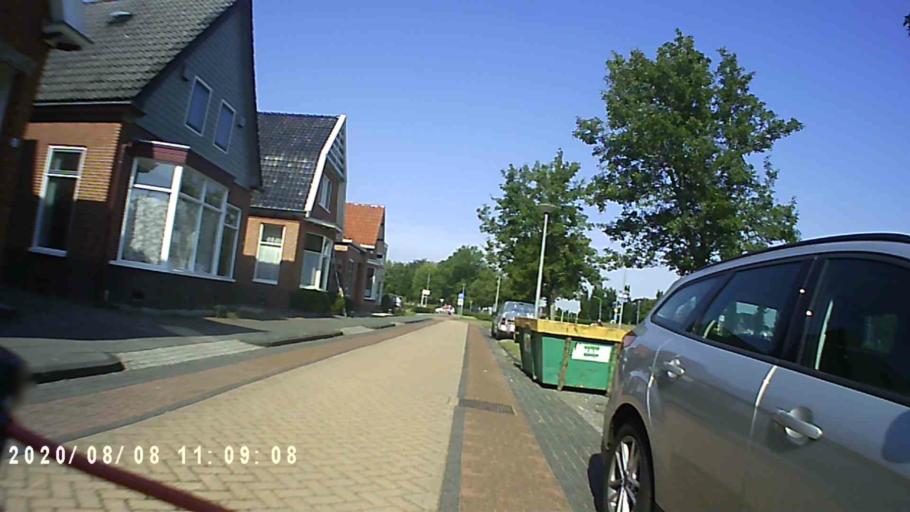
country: NL
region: Groningen
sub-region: Gemeente Leek
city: Leek
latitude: 53.1667
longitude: 6.3824
